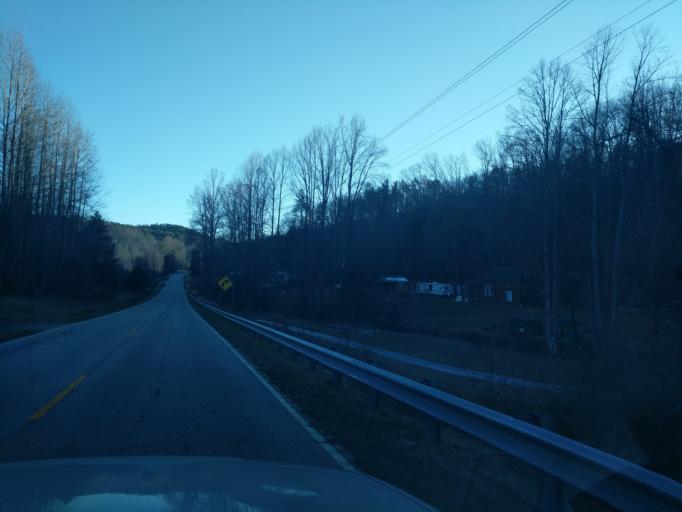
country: US
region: South Carolina
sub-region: Oconee County
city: Westminster
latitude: 34.7488
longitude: -83.2386
